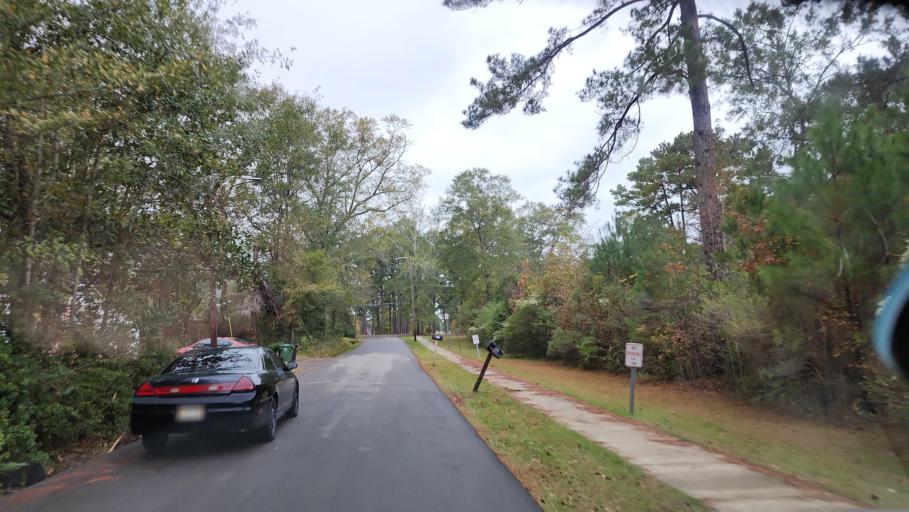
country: US
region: Mississippi
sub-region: Forrest County
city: Hattiesburg
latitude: 31.3033
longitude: -89.3024
